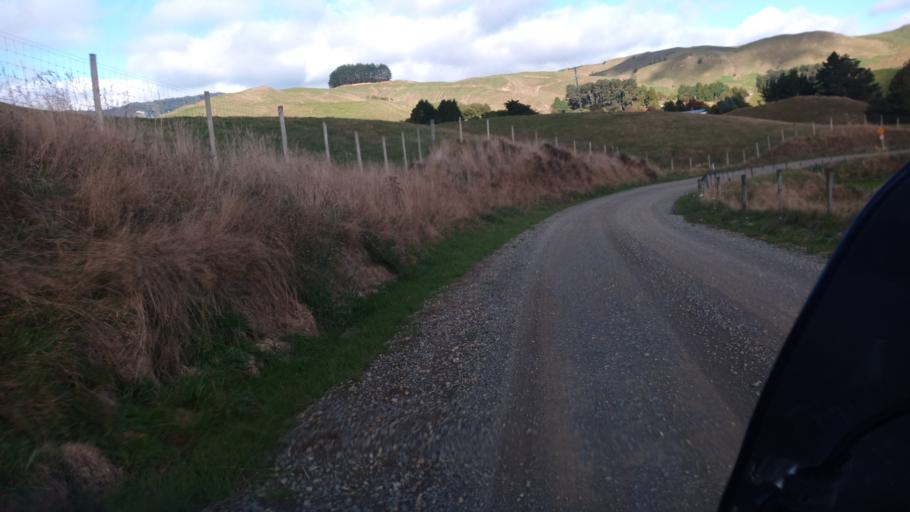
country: NZ
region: Bay of Plenty
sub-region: Opotiki District
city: Opotiki
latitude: -38.4588
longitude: 177.3894
